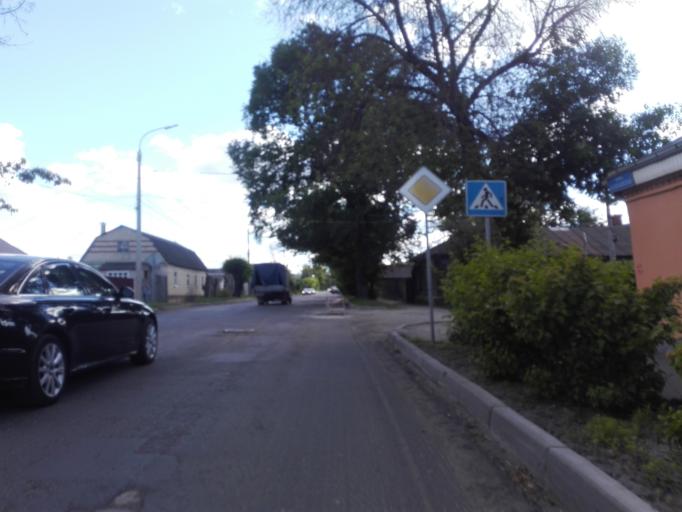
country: RU
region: Orjol
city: Orel
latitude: 52.9561
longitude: 36.0522
